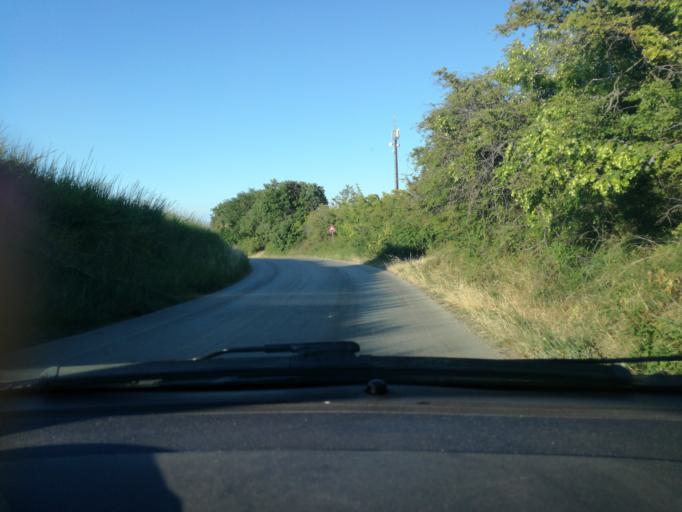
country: IT
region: Molise
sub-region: Provincia di Campobasso
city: Guglionesi
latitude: 41.9266
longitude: 14.9240
